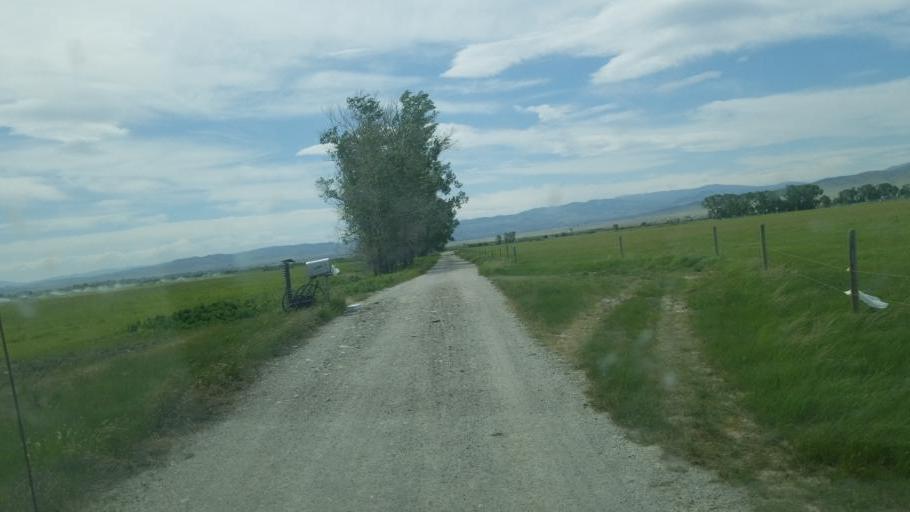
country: US
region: Montana
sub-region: Broadwater County
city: Townsend
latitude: 46.1834
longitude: -111.4726
